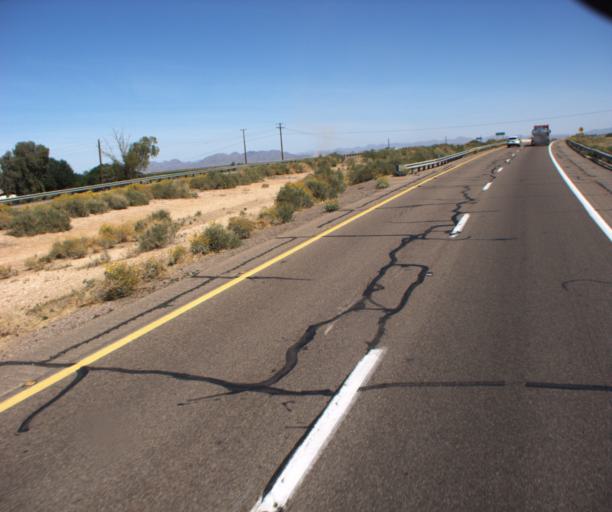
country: US
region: Arizona
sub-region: Maricopa County
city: Gila Bend
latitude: 32.9213
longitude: -112.8898
